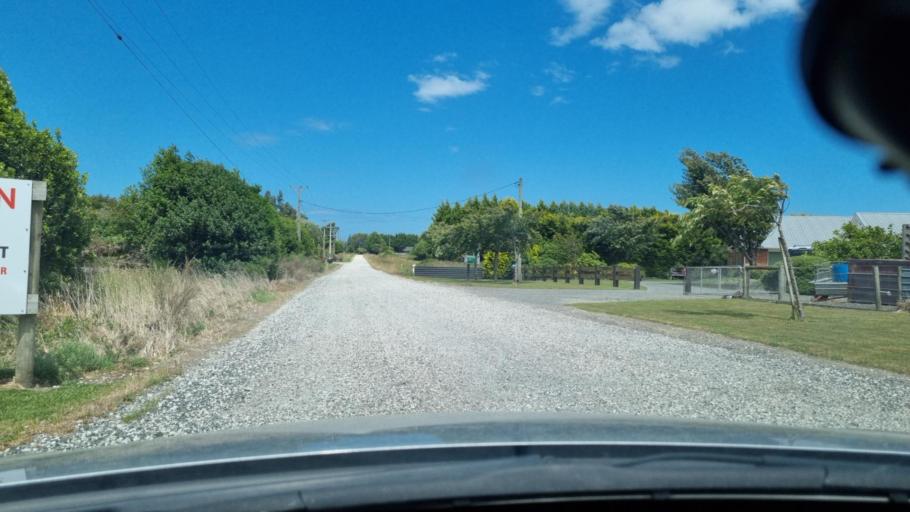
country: NZ
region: Southland
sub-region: Invercargill City
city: Invercargill
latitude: -46.4511
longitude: 168.3769
